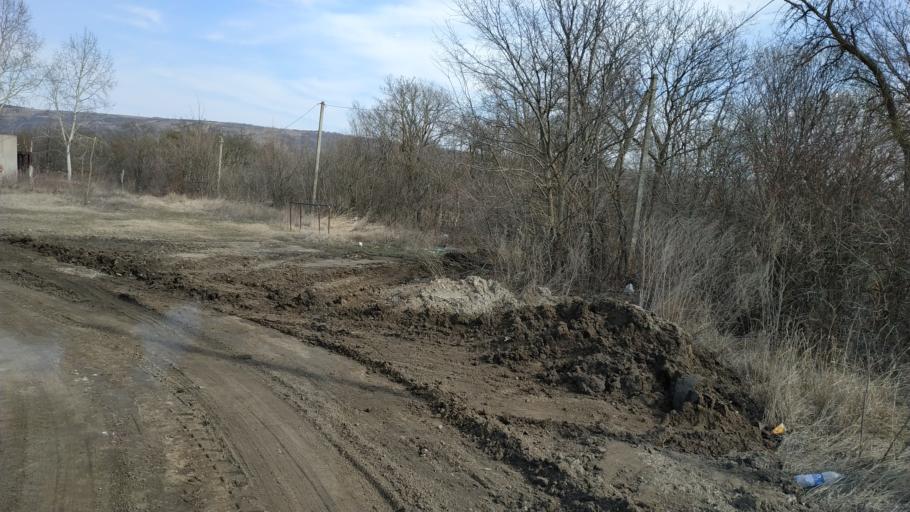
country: MD
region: Nisporeni
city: Nisporeni
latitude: 47.1929
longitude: 28.0670
